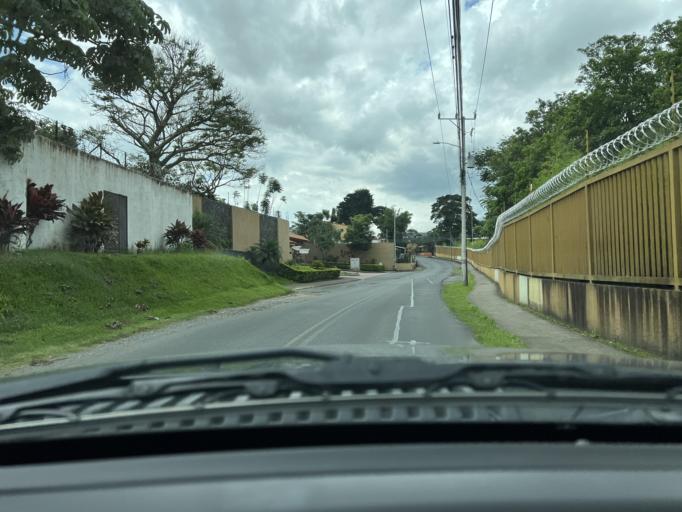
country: CR
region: San Jose
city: Granadilla
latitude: 9.9347
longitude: -84.0290
